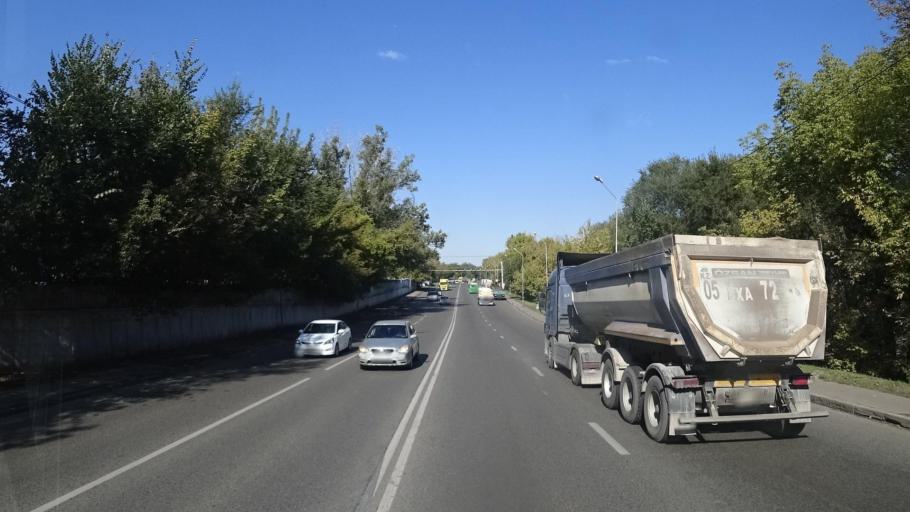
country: KZ
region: Almaty Oblysy
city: Pervomayskiy
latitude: 43.3431
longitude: 76.9762
